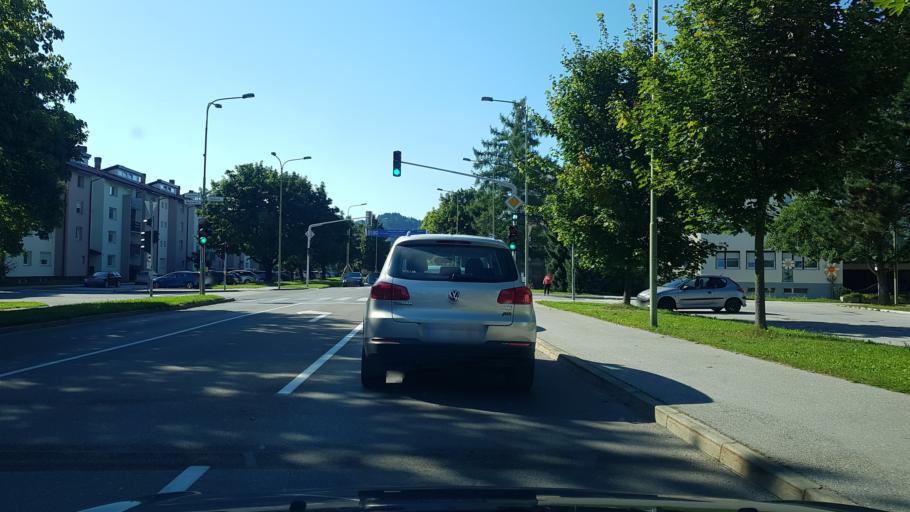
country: SI
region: Slovenj Gradec
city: Slovenj Gradec
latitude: 46.5043
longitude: 15.0841
